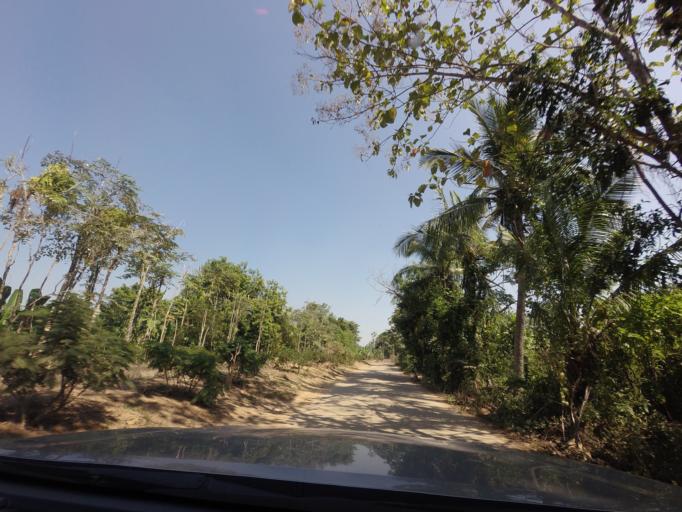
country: TH
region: Sukhothai
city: Sawankhalok
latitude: 17.2764
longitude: 99.8245
